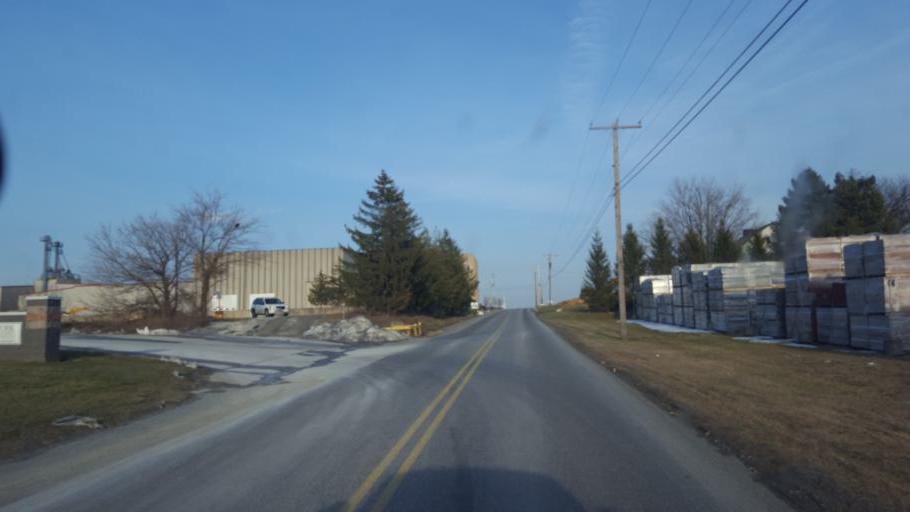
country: US
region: Pennsylvania
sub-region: Lancaster County
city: Blue Ball
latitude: 40.1079
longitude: -76.0611
